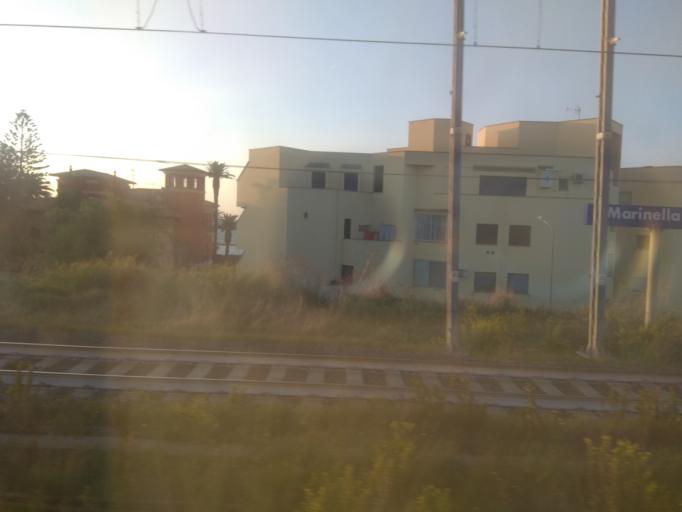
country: IT
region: Latium
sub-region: Citta metropolitana di Roma Capitale
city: Santa Marinella
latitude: 42.0355
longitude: 11.8603
